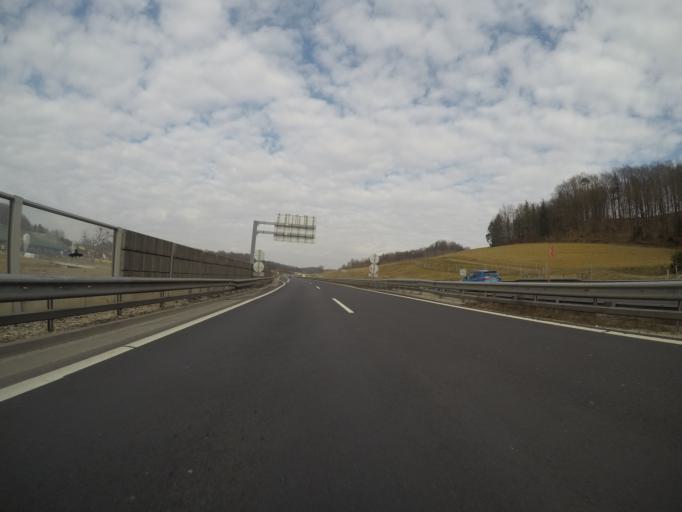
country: SI
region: Cerkvenjak
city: Cerkvenjak
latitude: 46.5584
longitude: 15.9177
